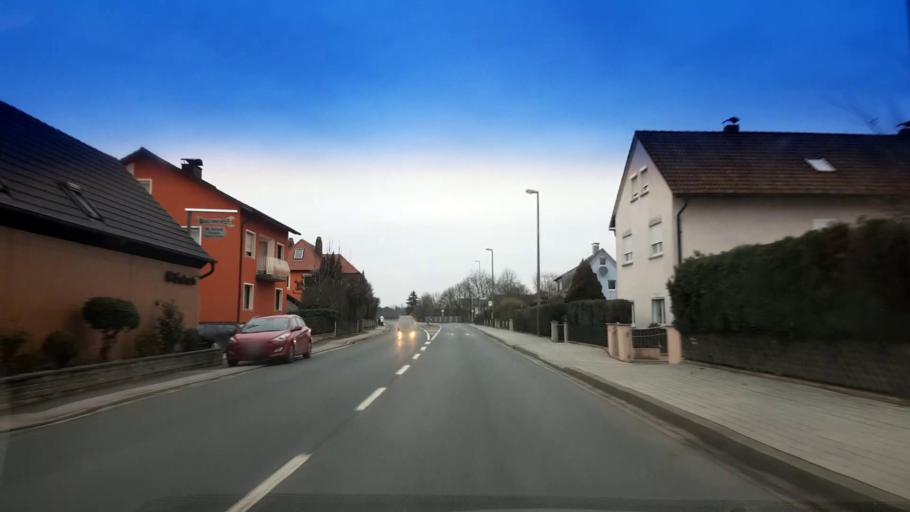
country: DE
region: Bavaria
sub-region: Upper Franconia
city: Altendorf
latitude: 49.7983
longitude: 11.0103
